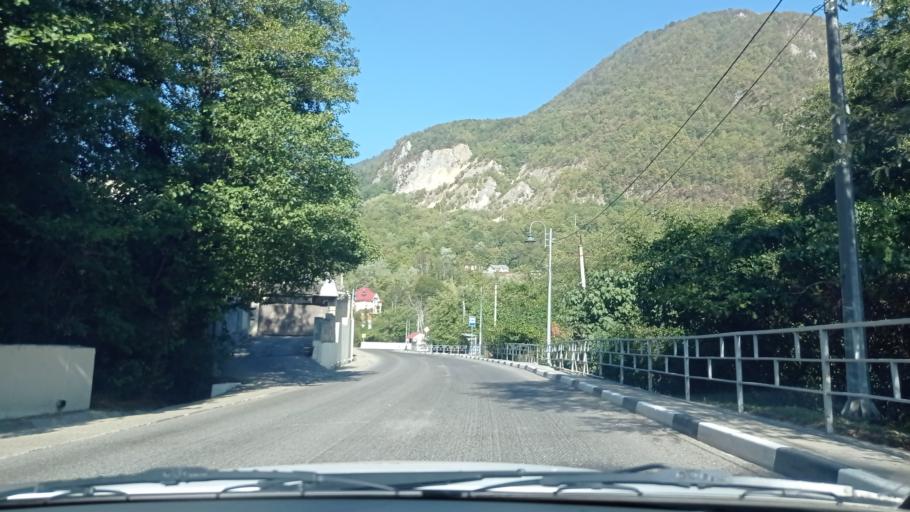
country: RU
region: Krasnodarskiy
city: Vysokoye
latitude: 43.5889
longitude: 40.0076
